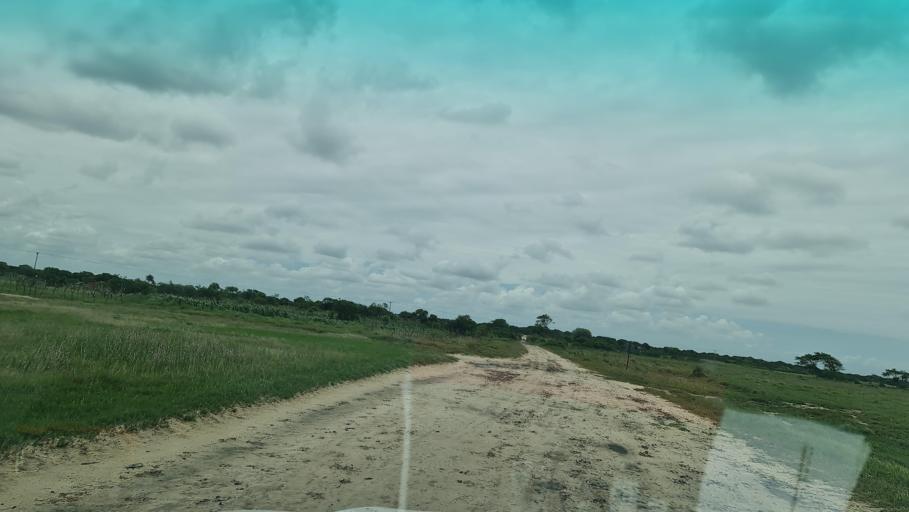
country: MZ
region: Maputo City
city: Maputo
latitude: -25.7034
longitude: 32.7041
